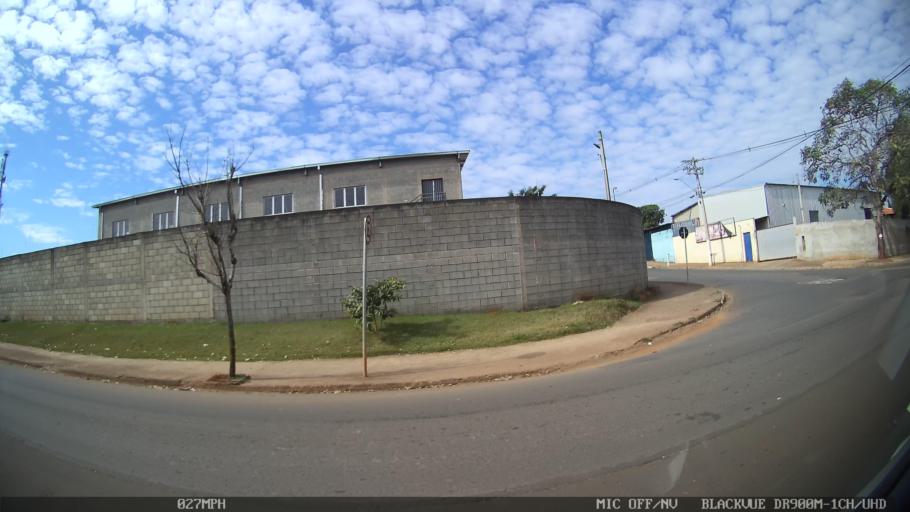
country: BR
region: Sao Paulo
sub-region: Santa Barbara D'Oeste
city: Santa Barbara d'Oeste
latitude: -22.7700
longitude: -47.4040
